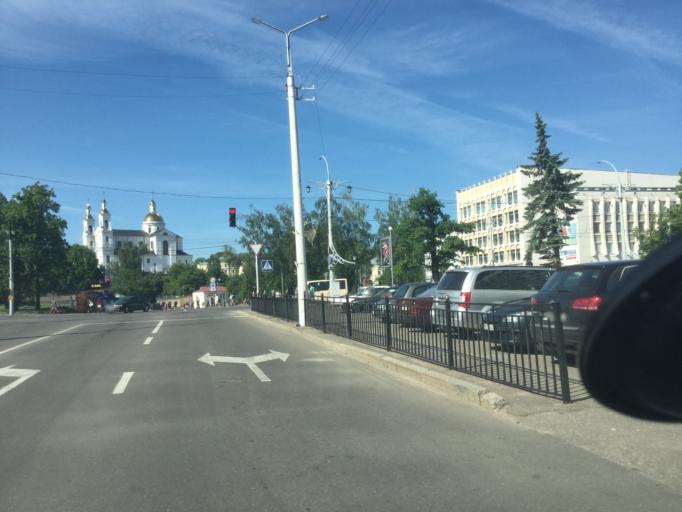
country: BY
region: Vitebsk
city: Vitebsk
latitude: 55.1924
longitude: 30.2021
